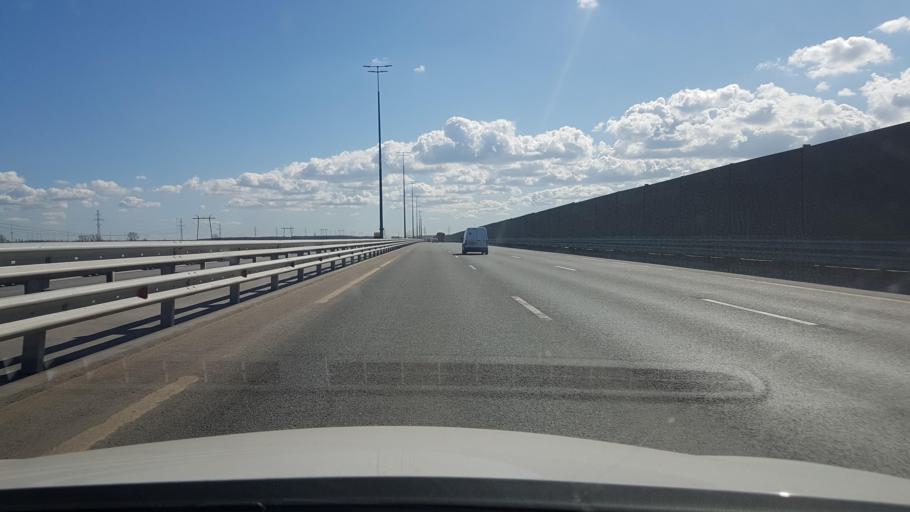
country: RU
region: Leningrad
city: Fedorovskoye
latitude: 59.6863
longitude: 30.5819
